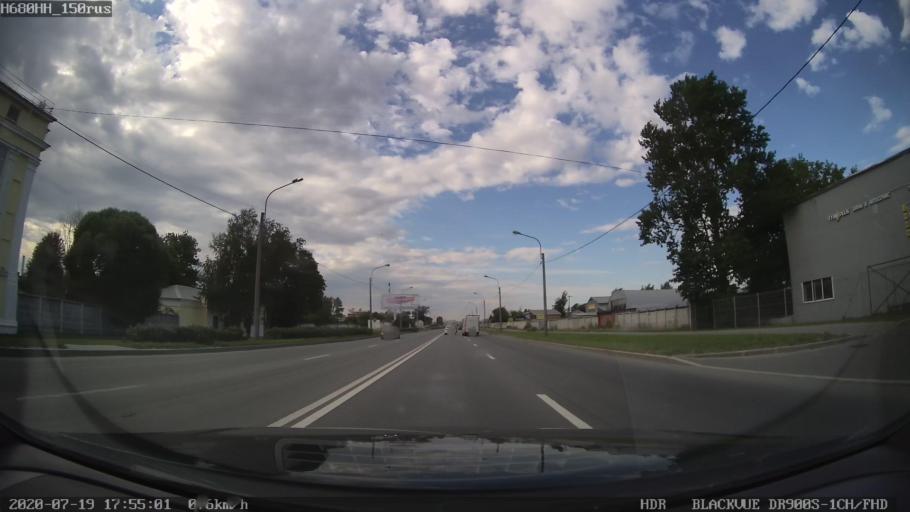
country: RU
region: St.-Petersburg
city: Admiralteisky
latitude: 59.8905
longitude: 30.3022
